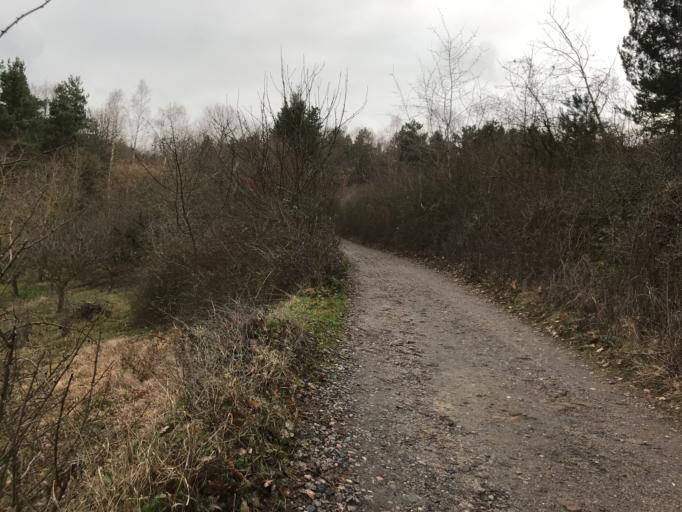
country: DE
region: Rheinland-Pfalz
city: Wachenheim
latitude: 49.4345
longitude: 8.1706
